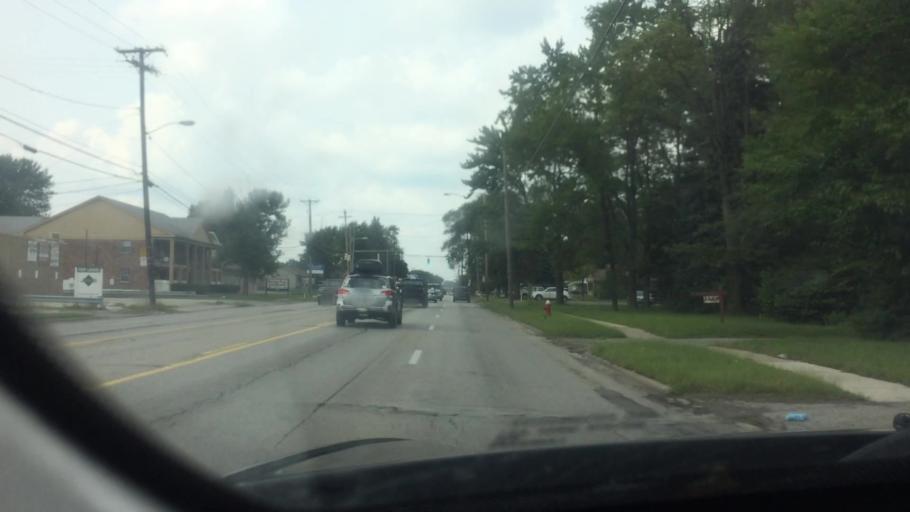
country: US
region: Ohio
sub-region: Lucas County
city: Ottawa Hills
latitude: 41.7122
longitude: -83.6238
